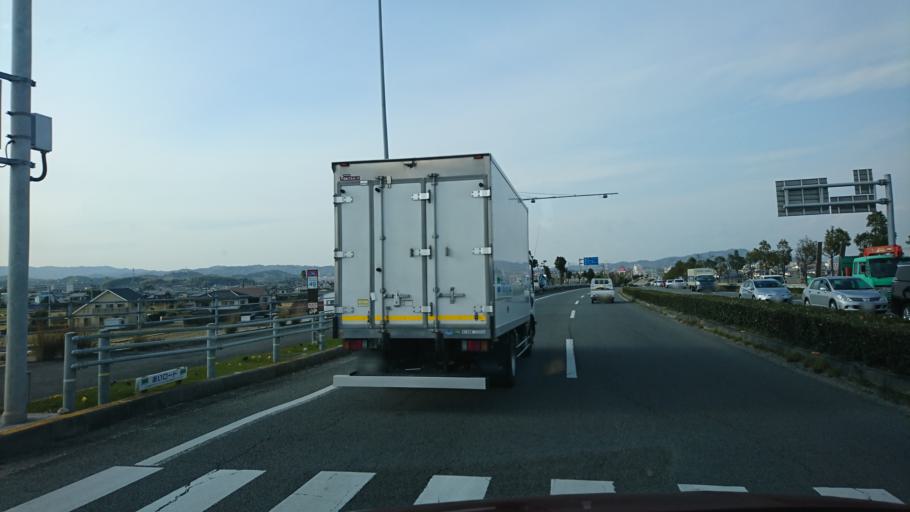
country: JP
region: Ehime
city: Saijo
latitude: 34.0222
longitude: 133.0111
